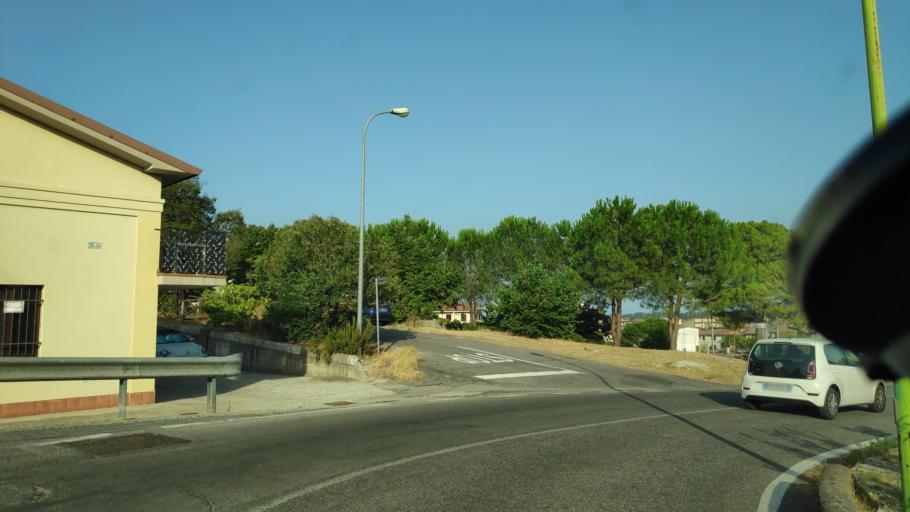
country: IT
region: Calabria
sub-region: Provincia di Catanzaro
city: Sant'Andrea Ionio Marina
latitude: 38.6200
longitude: 16.5480
